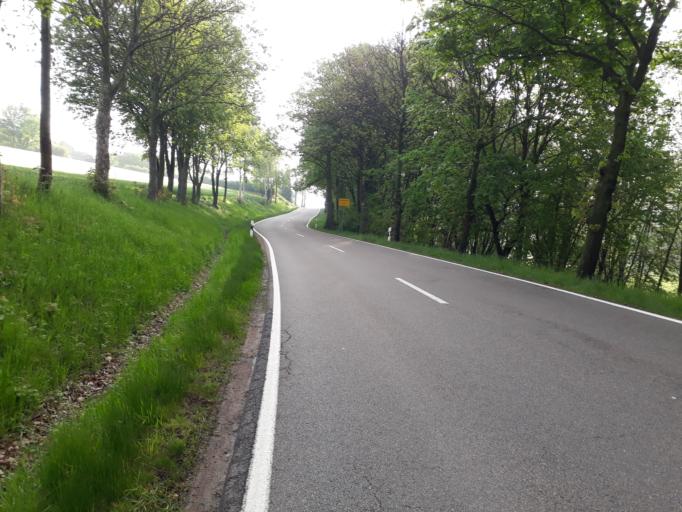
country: DE
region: Saxony
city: Reinhardtsgrimma
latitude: 50.8888
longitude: 13.7414
